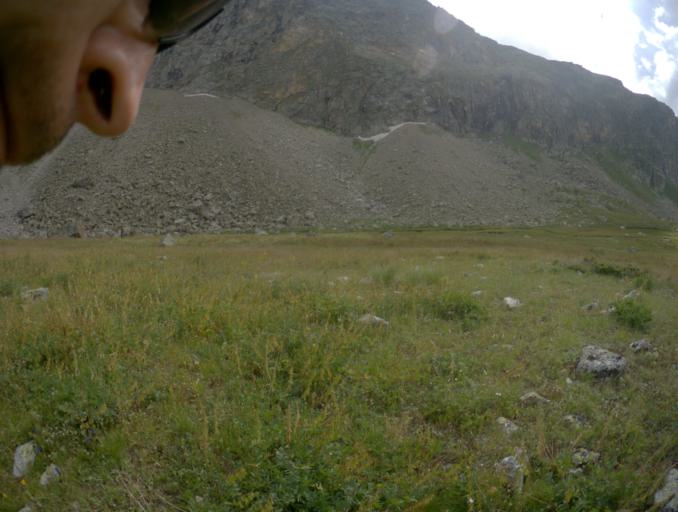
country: RU
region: Karachayevo-Cherkesiya
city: Uchkulan
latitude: 43.2858
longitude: 42.0895
